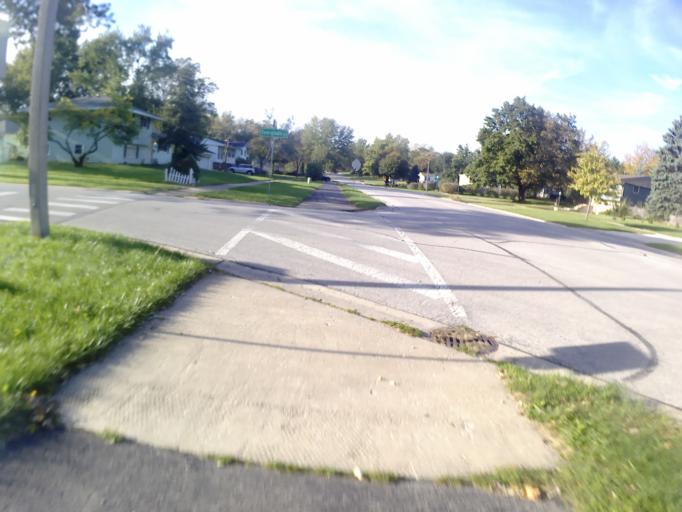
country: US
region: Illinois
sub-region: DuPage County
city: Woodridge
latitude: 41.7441
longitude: -88.0482
